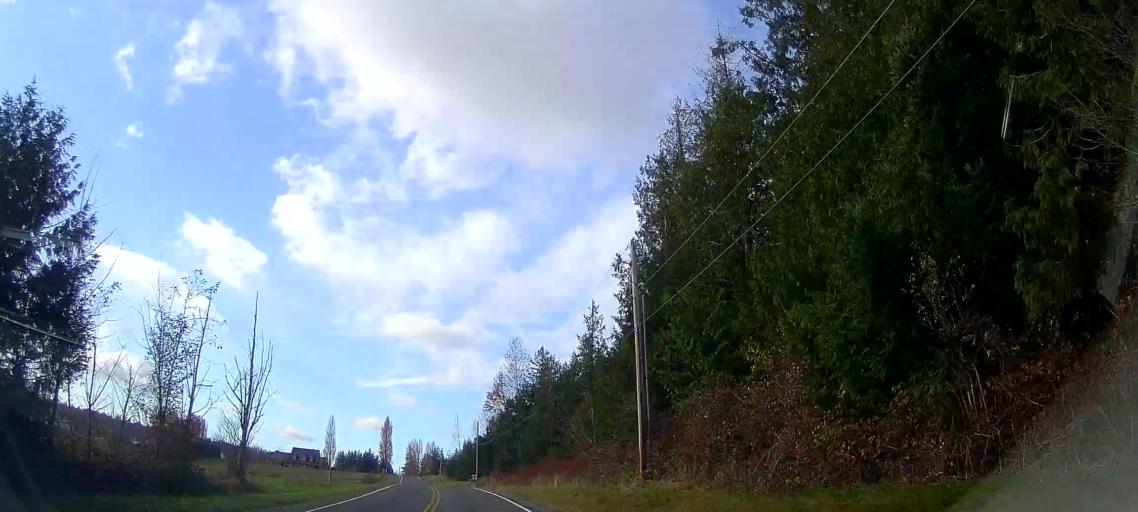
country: US
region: Washington
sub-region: Skagit County
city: Big Lake
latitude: 48.4169
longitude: -122.2287
